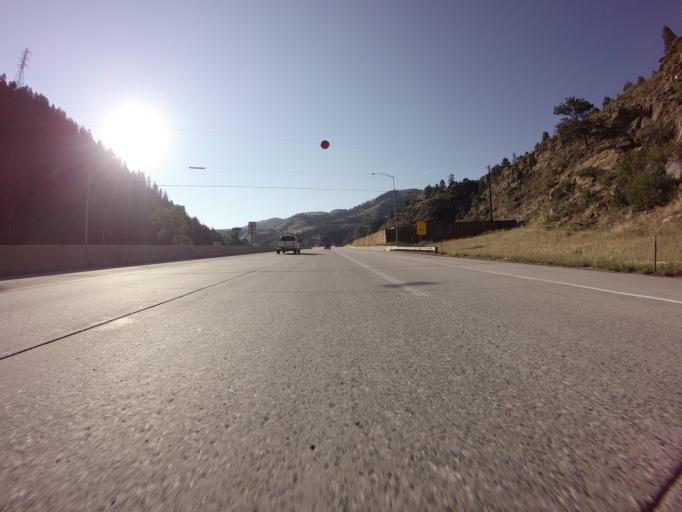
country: US
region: Colorado
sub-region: Clear Creek County
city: Idaho Springs
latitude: 39.7447
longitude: -105.4566
